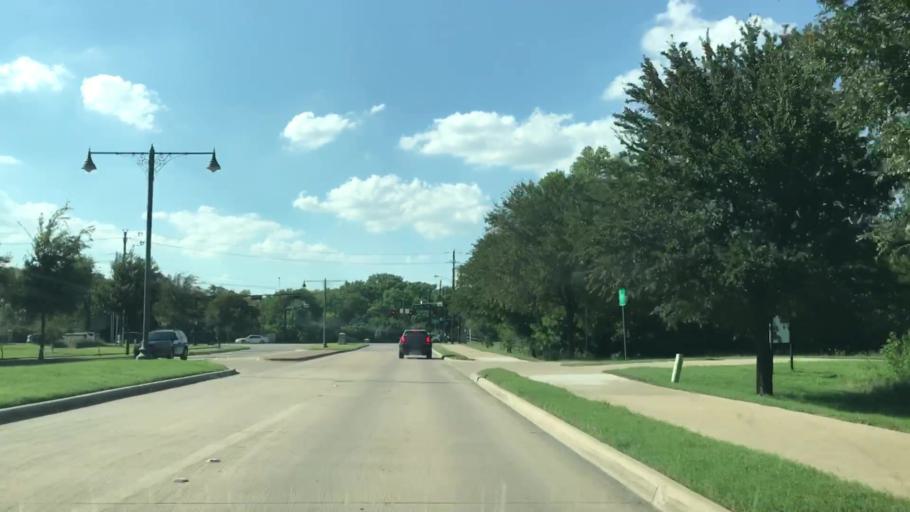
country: US
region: Texas
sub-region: Tarrant County
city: Keller
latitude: 32.9265
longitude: -97.2192
